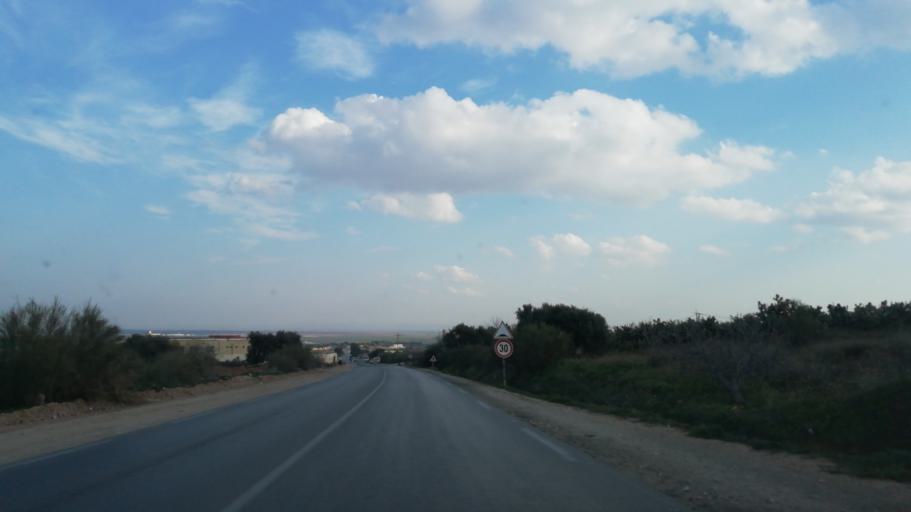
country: DZ
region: Relizane
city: Relizane
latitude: 35.9054
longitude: 0.5133
